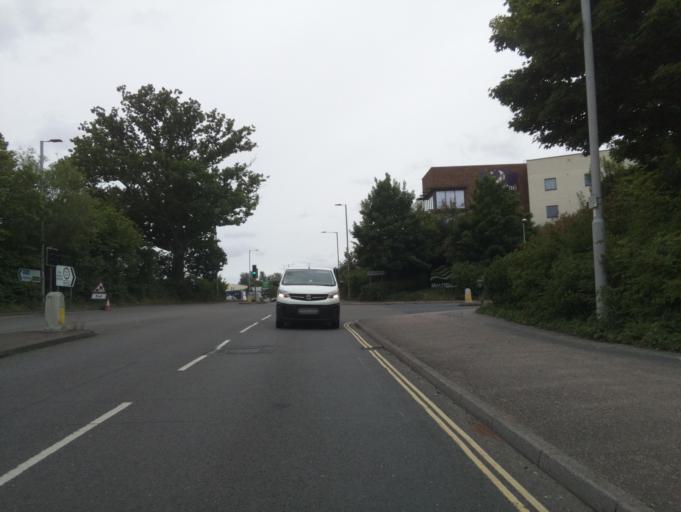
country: GB
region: England
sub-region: Devon
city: Heavitree
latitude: 50.7248
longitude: -3.4724
